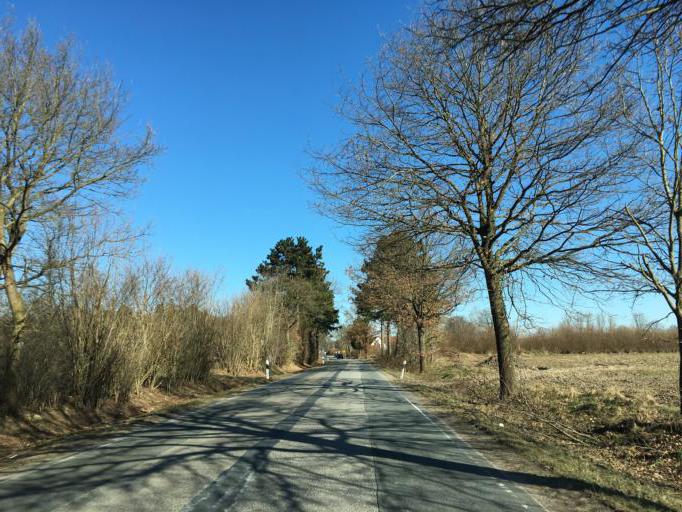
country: DE
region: Schleswig-Holstein
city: Lehmrade
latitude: 53.5875
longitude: 10.7531
